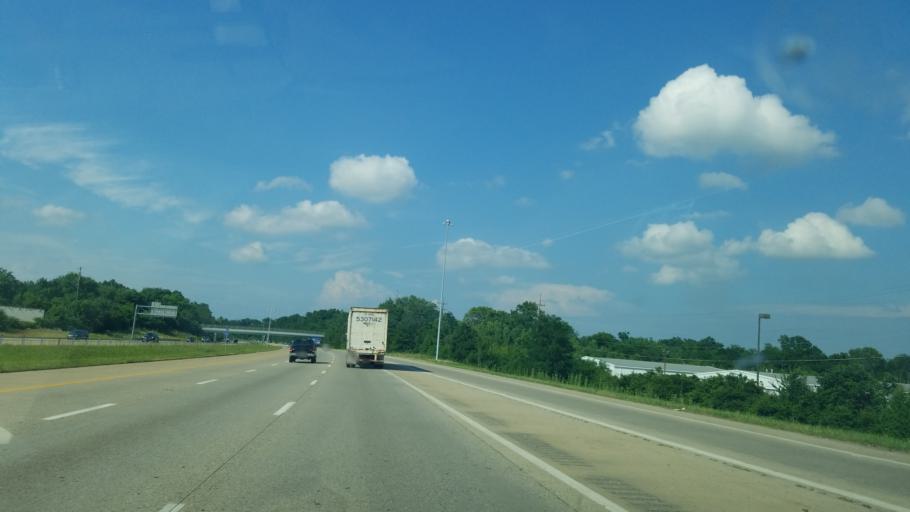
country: US
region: Ohio
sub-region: Clermont County
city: Withamsville
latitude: 39.0707
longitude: -84.2965
